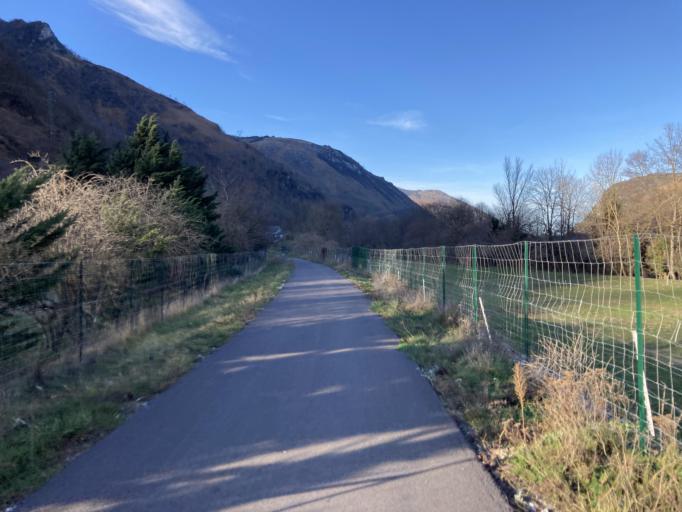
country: FR
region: Aquitaine
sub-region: Departement des Pyrenees-Atlantiques
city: Laruns
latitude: 43.0067
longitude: -0.4197
